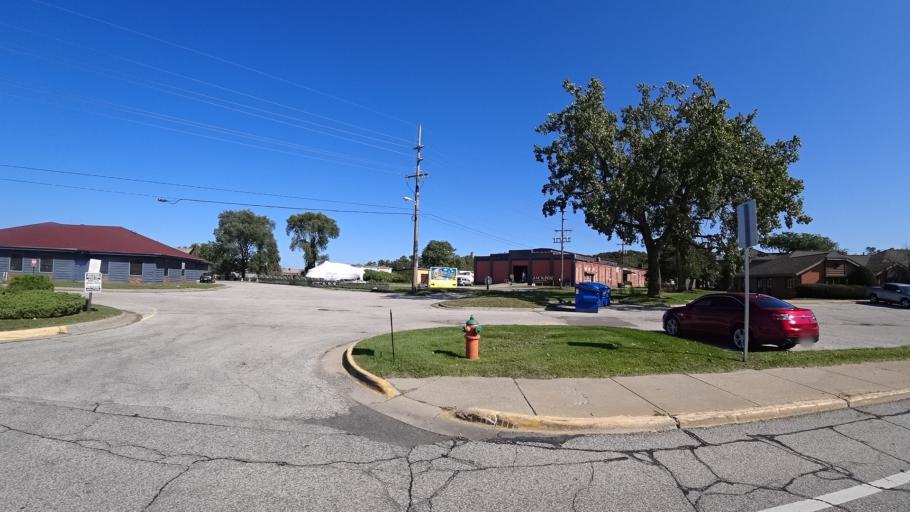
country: US
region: Indiana
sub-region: LaPorte County
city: Michigan City
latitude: 41.7208
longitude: -86.9022
